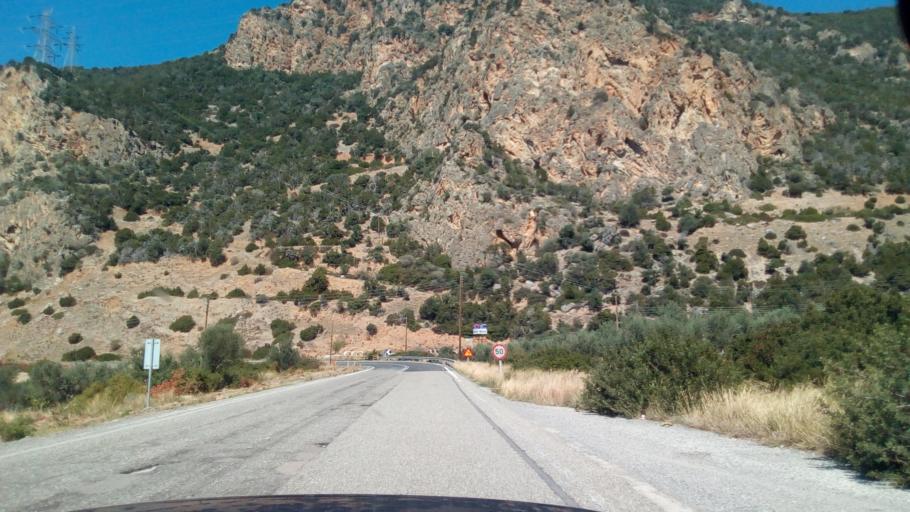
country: GR
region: West Greece
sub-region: Nomos Achaias
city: Aigio
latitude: 38.3574
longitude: 22.1397
